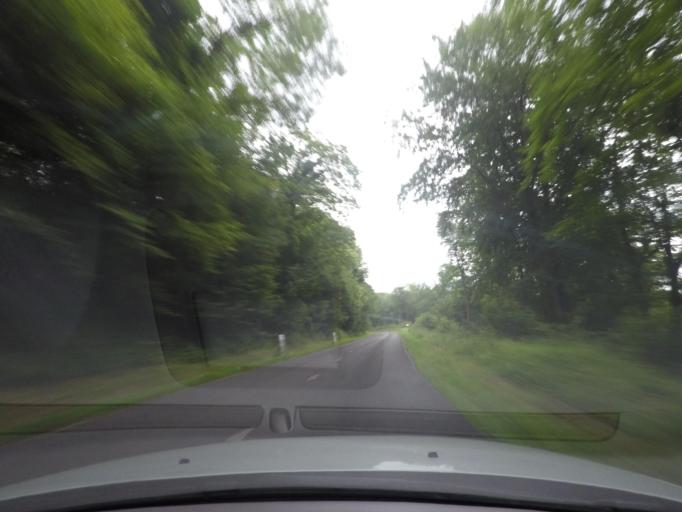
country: FR
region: Haute-Normandie
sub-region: Departement de la Seine-Maritime
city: Neufchatel-en-Bray
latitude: 49.7394
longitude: 1.4775
